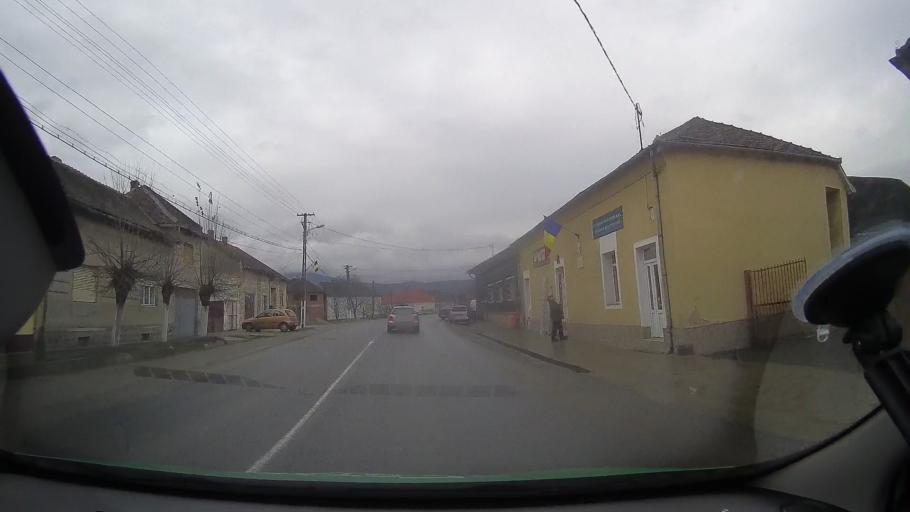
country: RO
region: Arad
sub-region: Comuna Buteni
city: Buteni
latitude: 46.3267
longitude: 22.1235
